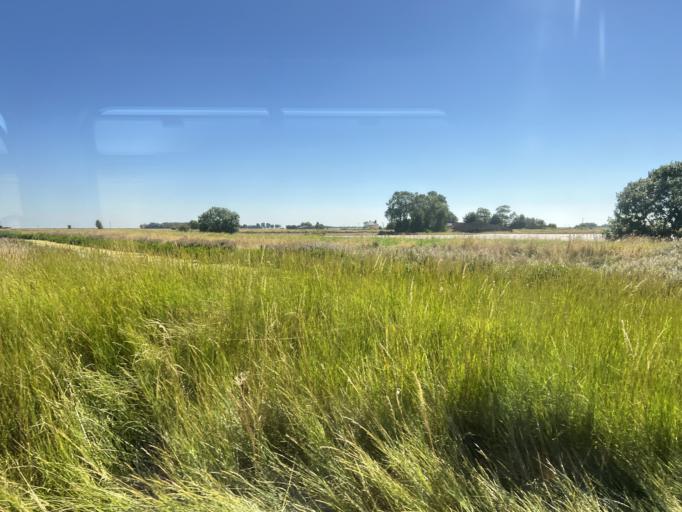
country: GB
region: England
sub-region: Lincolnshire
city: Wainfleet All Saints
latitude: 53.1110
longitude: 0.2619
